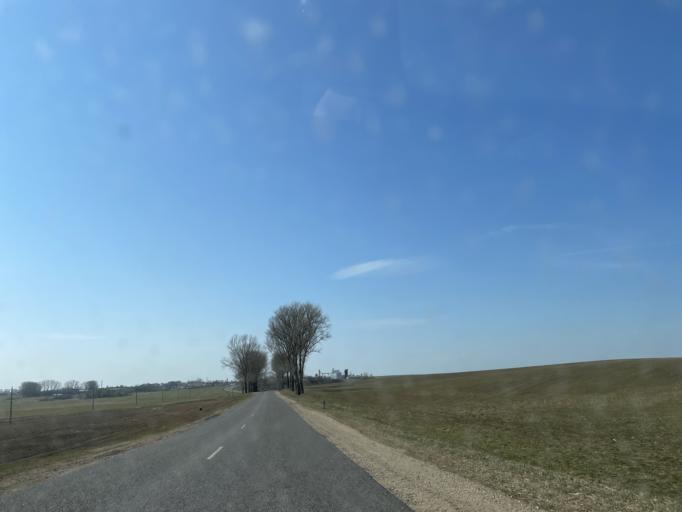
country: BY
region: Minsk
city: Snow
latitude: 53.1973
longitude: 26.4953
